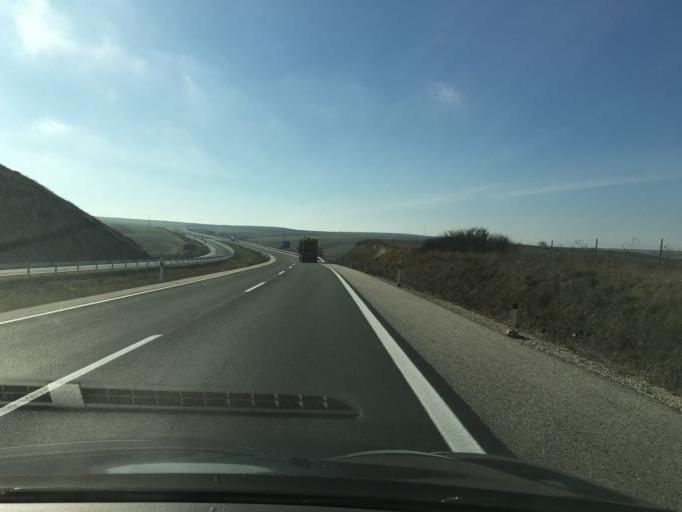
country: ES
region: Castille and Leon
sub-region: Provincia de Burgos
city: Zuneda
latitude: 42.6014
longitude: -3.2220
